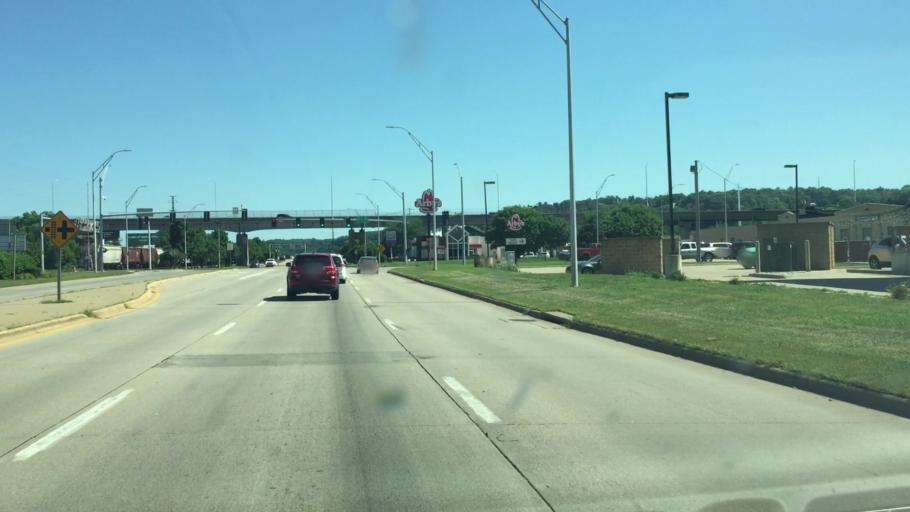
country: US
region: Iowa
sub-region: Dubuque County
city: Dubuque
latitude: 42.4938
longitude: -90.6625
